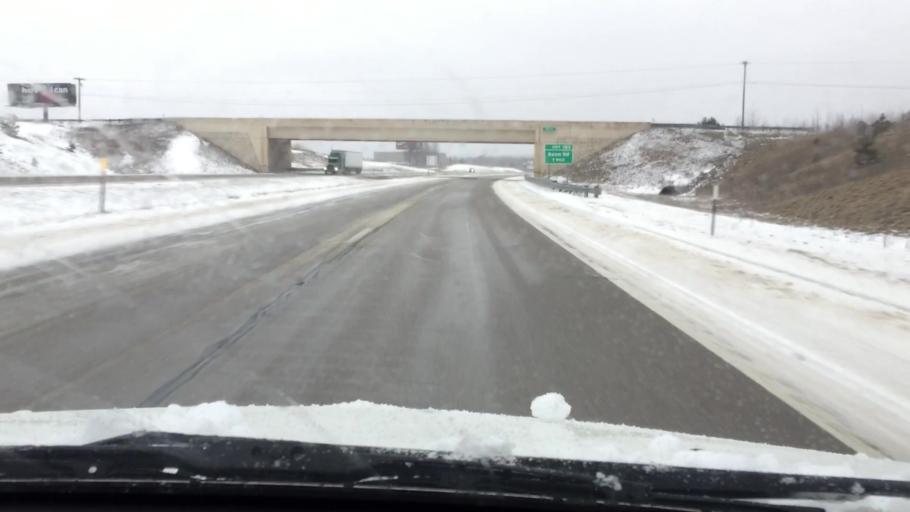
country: US
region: Michigan
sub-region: Wexford County
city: Cadillac
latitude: 44.2659
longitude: -85.3873
